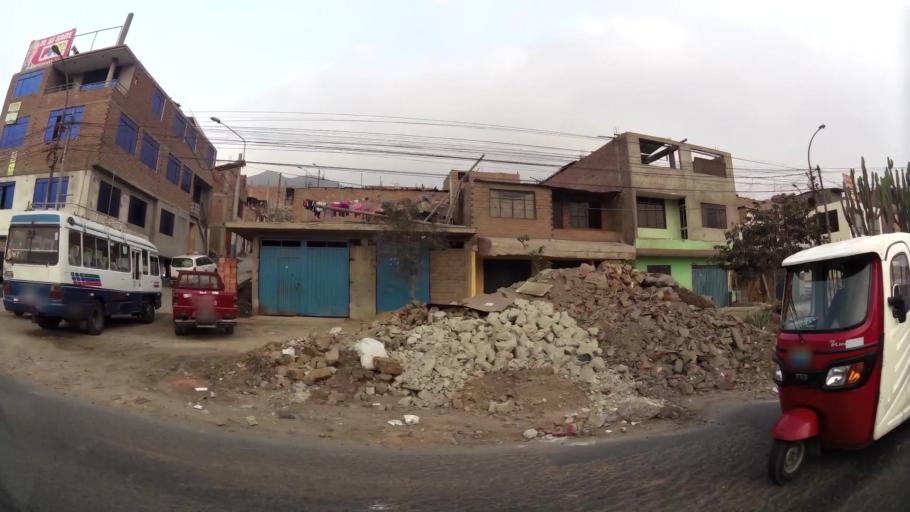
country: PE
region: Lima
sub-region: Lima
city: Independencia
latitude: -11.9897
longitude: -76.9991
